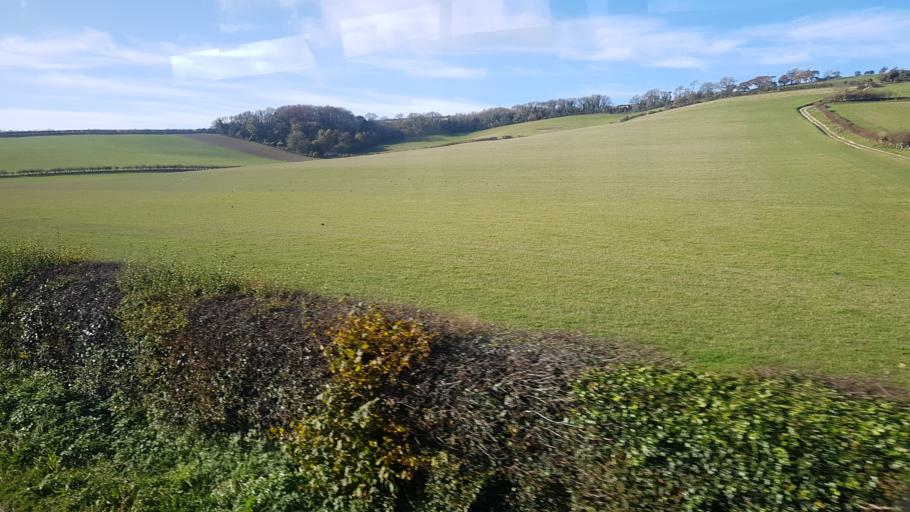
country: GB
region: England
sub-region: Isle of Wight
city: Newport
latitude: 50.6713
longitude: -1.3427
